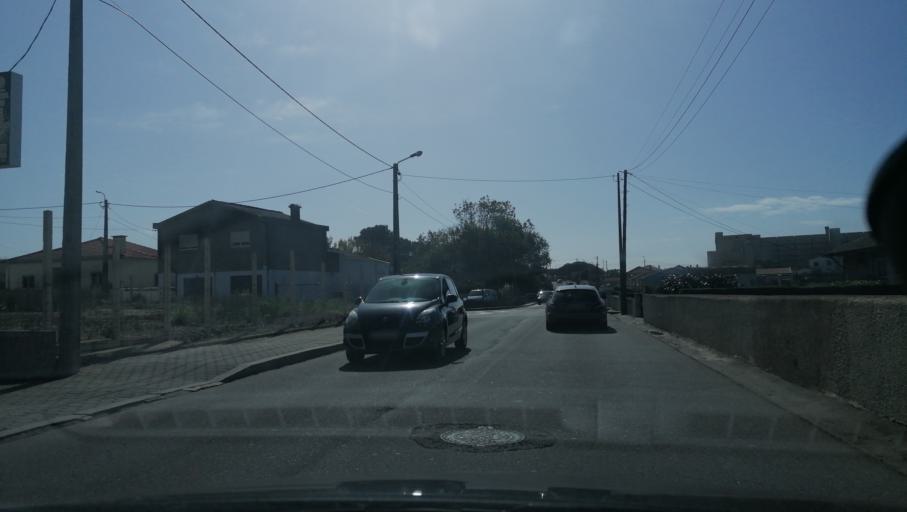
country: PT
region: Porto
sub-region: Vila Nova de Gaia
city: Arcozelo
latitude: 41.0330
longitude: -8.6438
